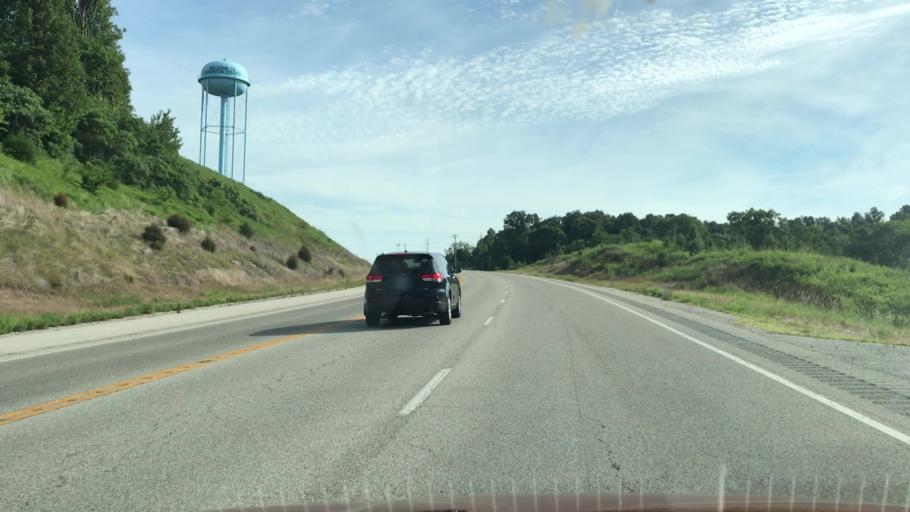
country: US
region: Kentucky
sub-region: Edmonson County
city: Brownsville
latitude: 37.0988
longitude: -86.2307
